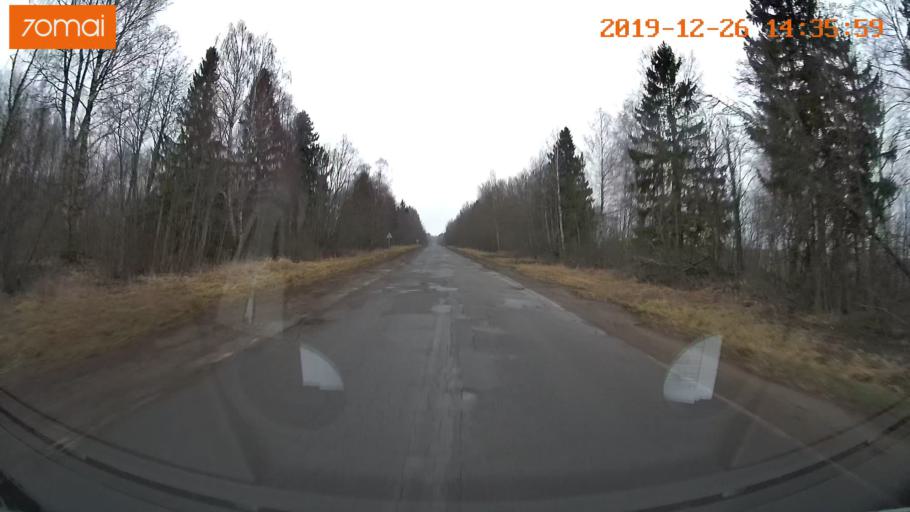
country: RU
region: Jaroslavl
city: Poshekhon'ye
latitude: 58.4158
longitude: 38.9780
